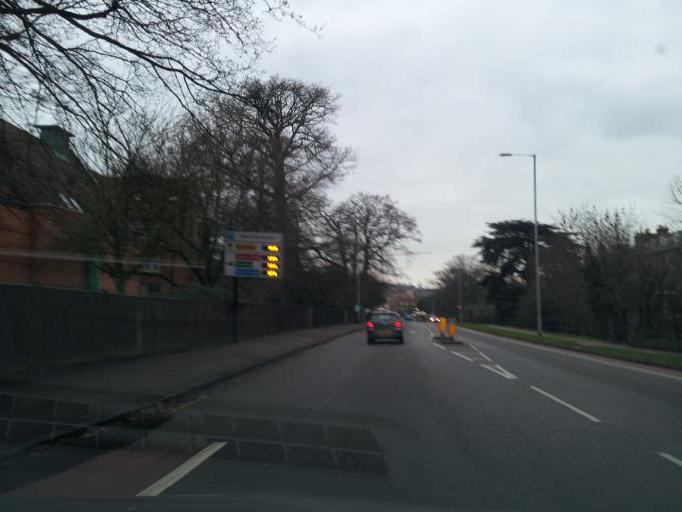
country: GB
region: England
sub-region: Cambridgeshire
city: Cambridge
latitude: 52.1956
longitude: 0.1223
